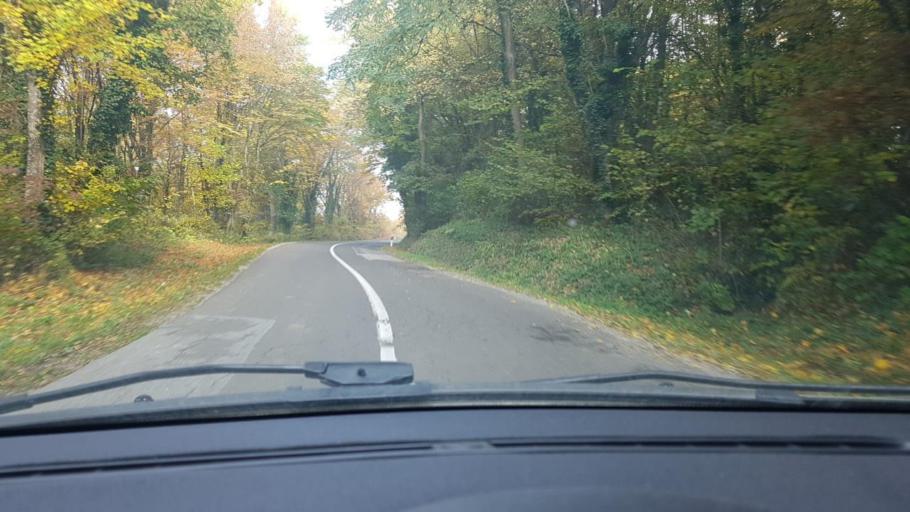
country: HR
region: Krapinsko-Zagorska
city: Zlatar
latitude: 46.1351
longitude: 16.1355
